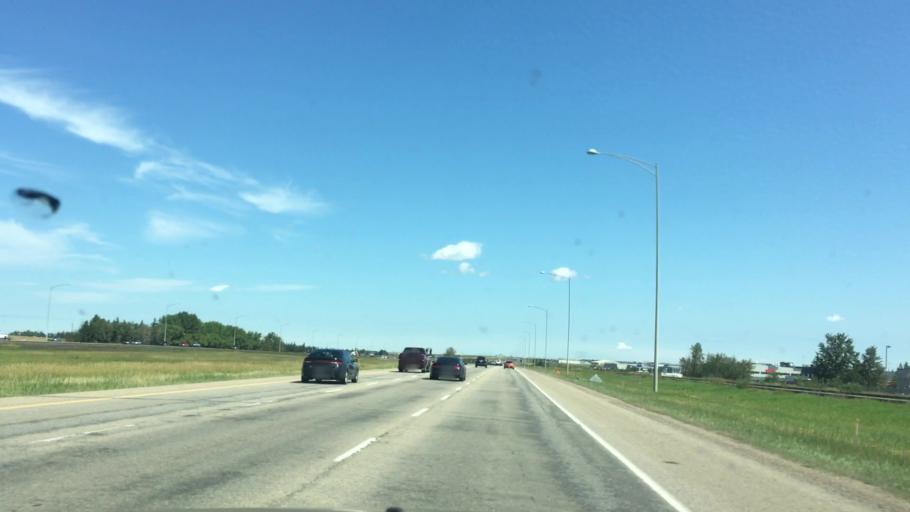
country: CA
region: Alberta
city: Leduc
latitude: 53.3677
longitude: -113.5283
